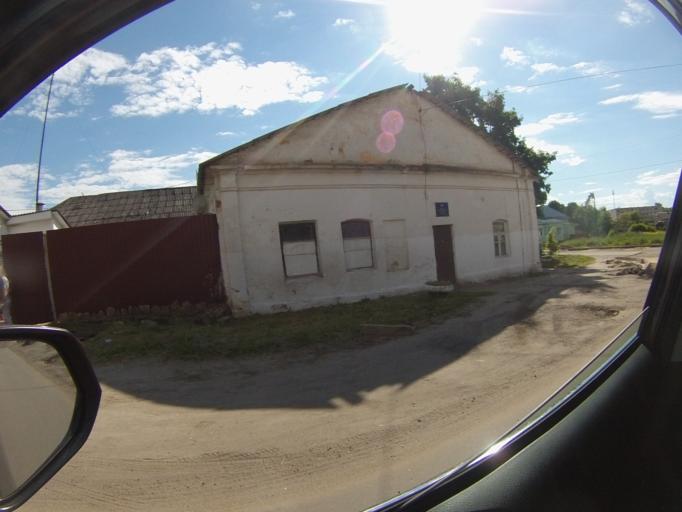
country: RU
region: Orjol
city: Mtsensk
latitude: 53.2772
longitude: 36.5697
